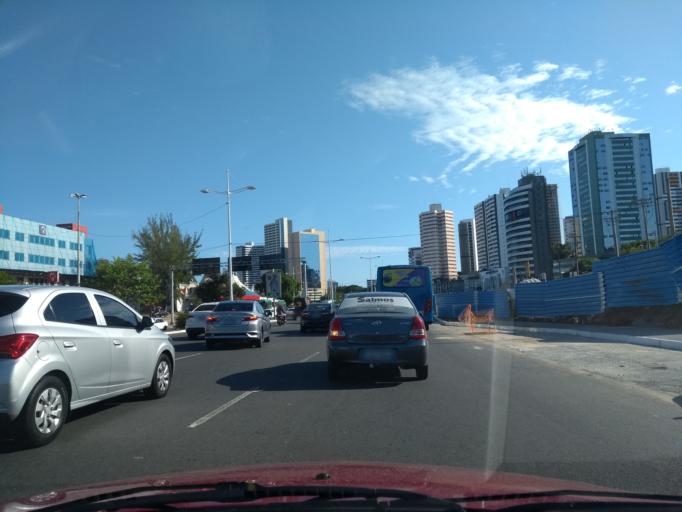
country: BR
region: Bahia
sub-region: Salvador
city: Salvador
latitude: -12.9824
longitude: -38.4663
